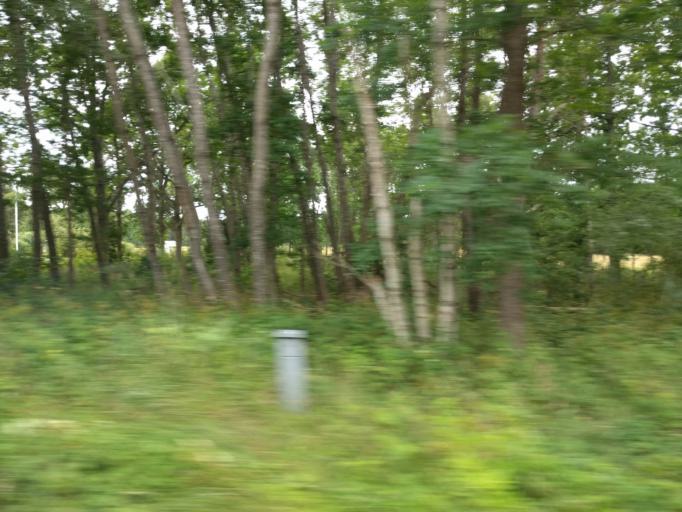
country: SE
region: Soedermanland
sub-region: Nykopings Kommun
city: Svalsta
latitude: 58.4951
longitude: 16.8925
